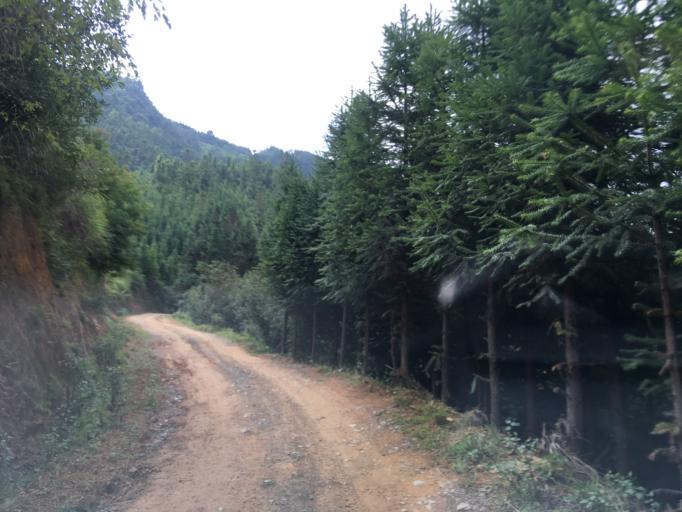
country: CN
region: Guangxi Zhuangzu Zizhiqu
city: Xinzhou
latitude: 24.8825
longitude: 105.8449
